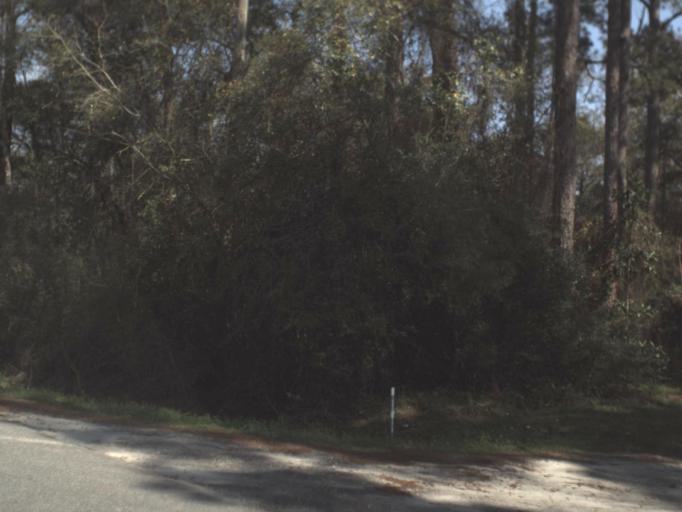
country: US
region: Florida
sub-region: Wakulla County
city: Crawfordville
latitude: 30.0608
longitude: -84.4749
